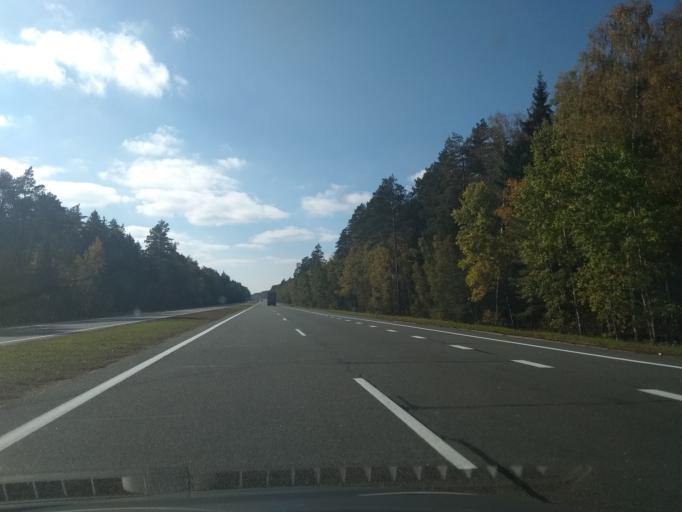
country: BY
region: Brest
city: Baranovichi
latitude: 53.0474
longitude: 25.8420
